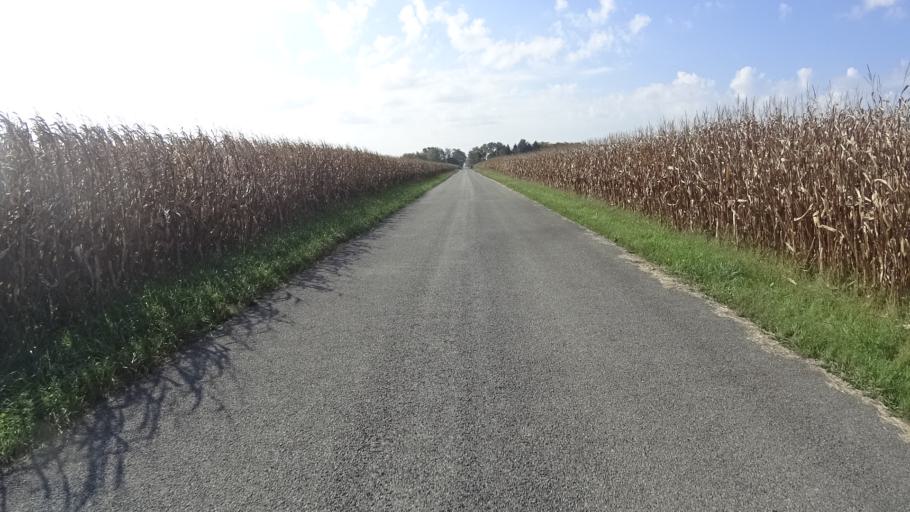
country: US
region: Indiana
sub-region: Madison County
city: Lapel
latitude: 40.0310
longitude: -85.8242
